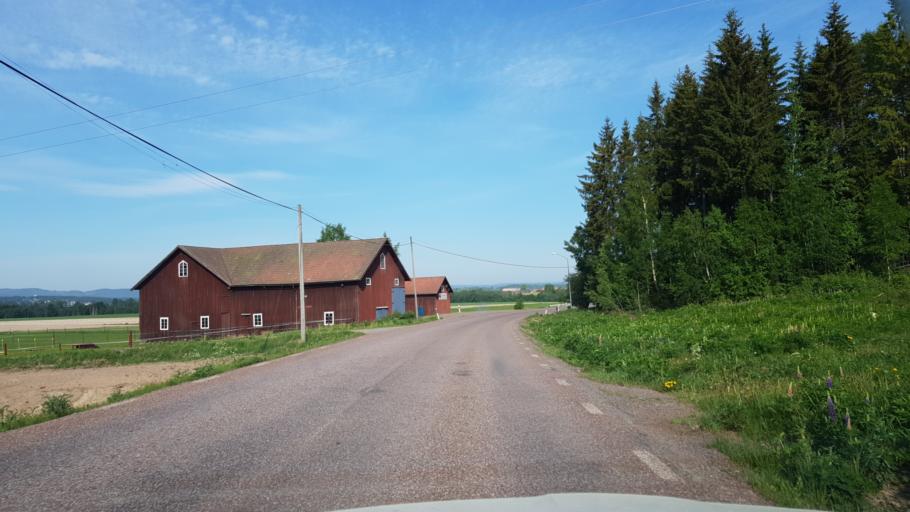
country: SE
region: Dalarna
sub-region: Saters Kommun
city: Saeter
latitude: 60.4149
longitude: 15.6777
